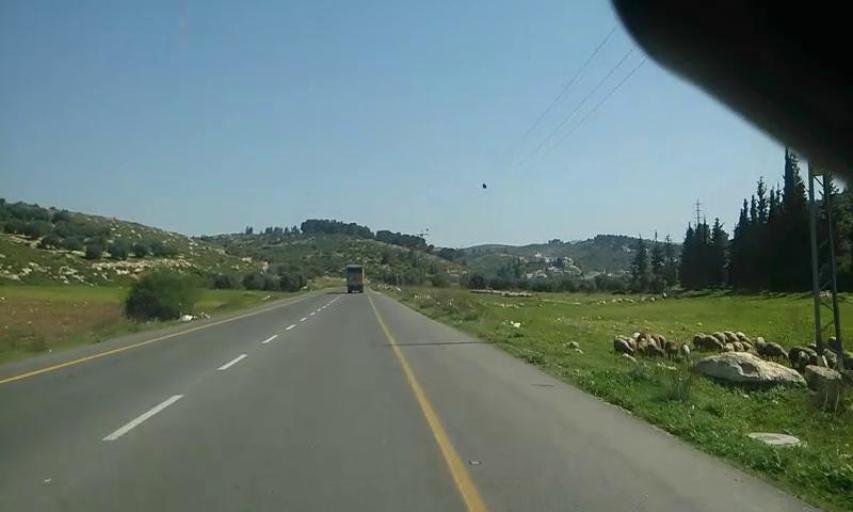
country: PS
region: West Bank
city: Idhna
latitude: 31.5752
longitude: 34.9810
